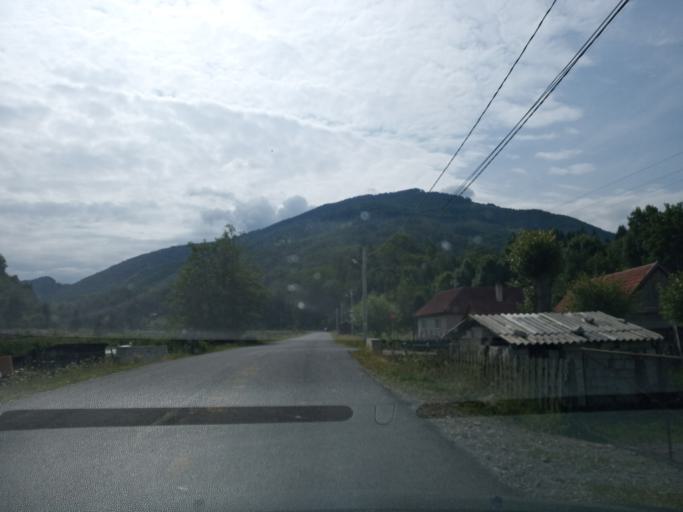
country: RO
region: Hunedoara
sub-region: Oras Petrila
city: Petrila
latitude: 45.4175
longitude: 23.4318
